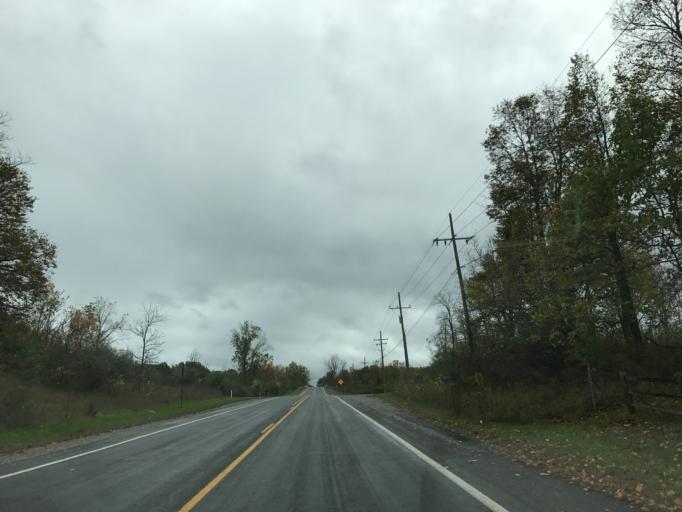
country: US
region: Michigan
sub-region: Washtenaw County
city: Ann Arbor
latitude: 42.3287
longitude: -83.6617
